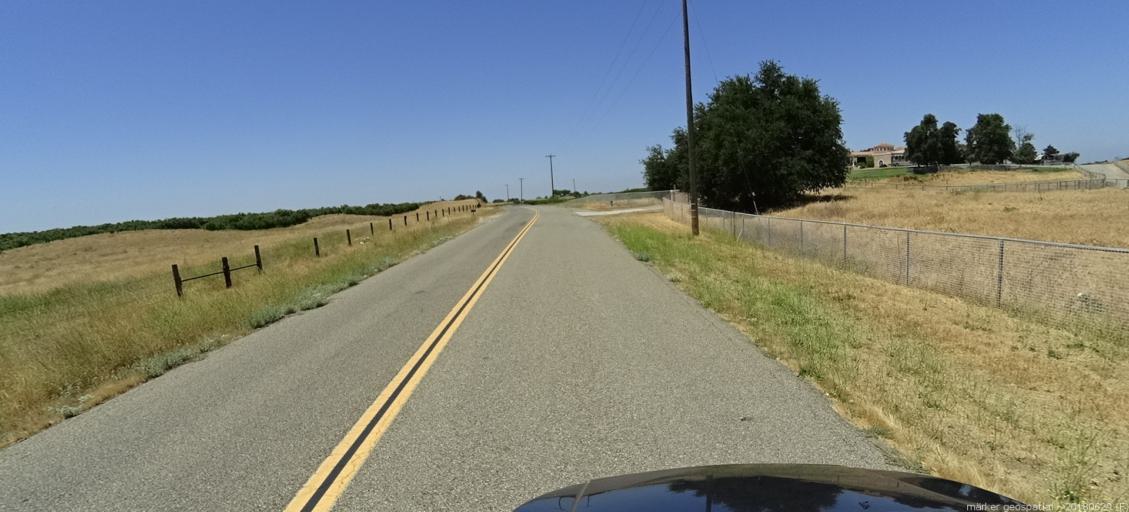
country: US
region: California
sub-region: Madera County
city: Parksdale
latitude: 37.0116
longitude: -119.9672
